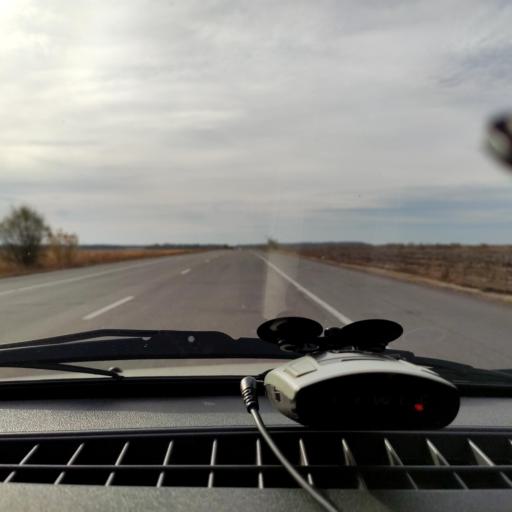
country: RU
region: Voronezj
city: Devitsa
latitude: 51.5898
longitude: 38.9774
